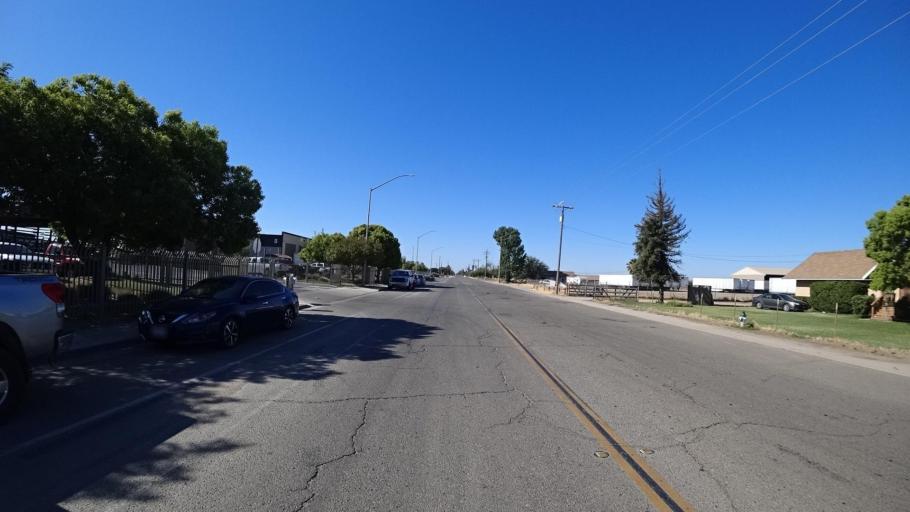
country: US
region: California
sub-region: Fresno County
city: Easton
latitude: 36.6899
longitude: -119.7818
